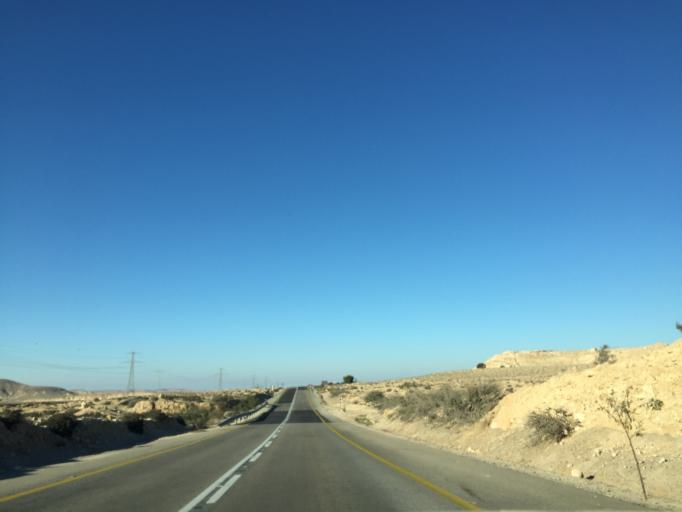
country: IL
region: Southern District
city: Midreshet Ben-Gurion
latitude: 30.7791
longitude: 34.7693
